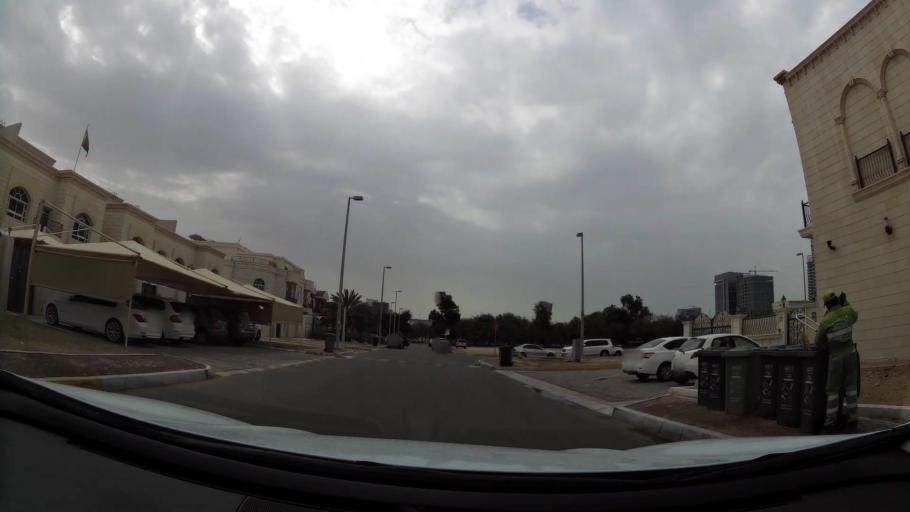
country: AE
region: Abu Dhabi
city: Abu Dhabi
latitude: 24.4332
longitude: 54.4416
